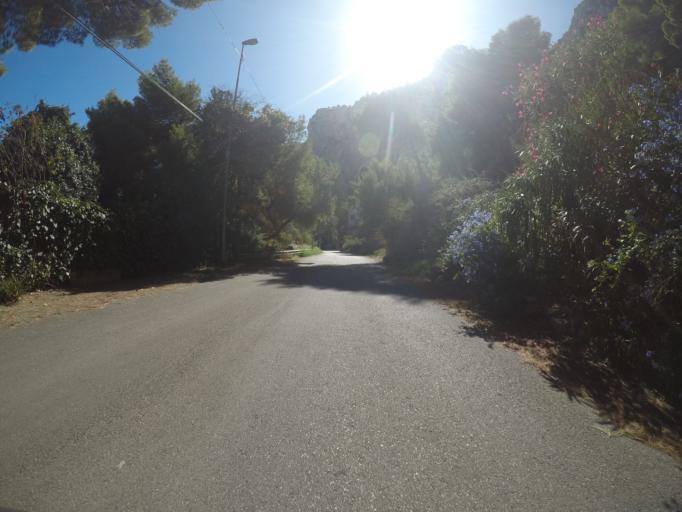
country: IT
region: Sicily
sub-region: Palermo
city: Palermo
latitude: 38.1878
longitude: 13.3434
